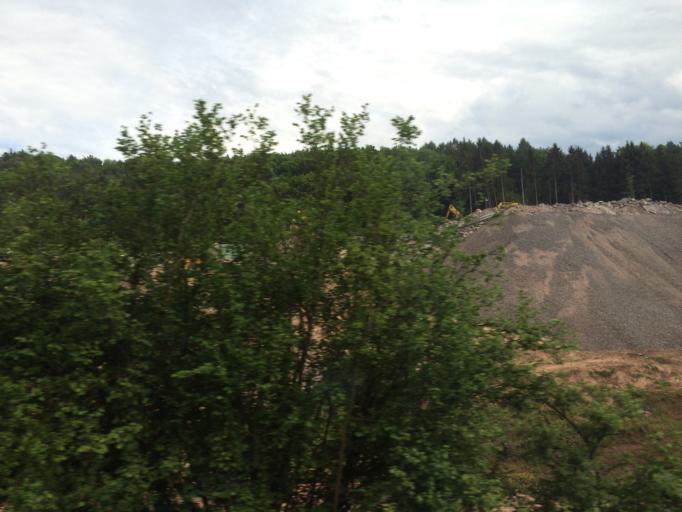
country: DE
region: Bavaria
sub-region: Regierungsbezirk Unterfranken
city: Laufach
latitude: 50.0118
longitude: 9.3376
